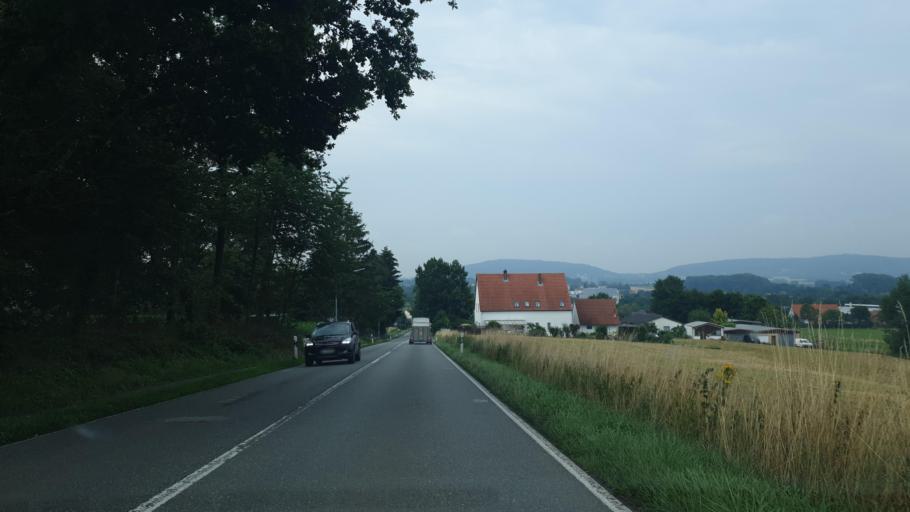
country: DE
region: North Rhine-Westphalia
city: Loehne
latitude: 52.2343
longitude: 8.7381
